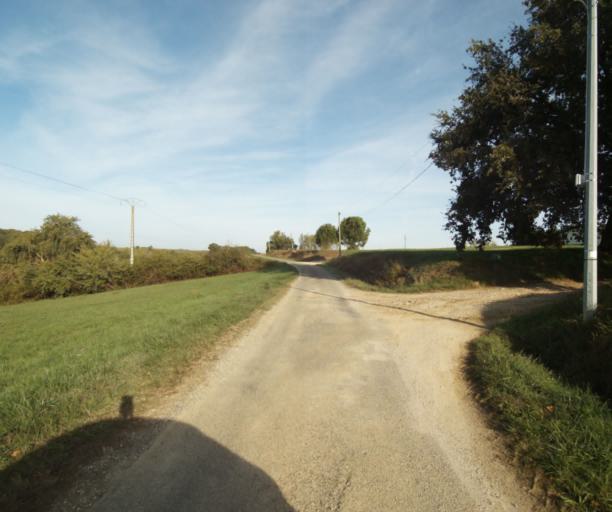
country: FR
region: Midi-Pyrenees
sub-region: Departement de la Haute-Garonne
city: Villemur-sur-Tarn
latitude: 43.9065
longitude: 1.5015
